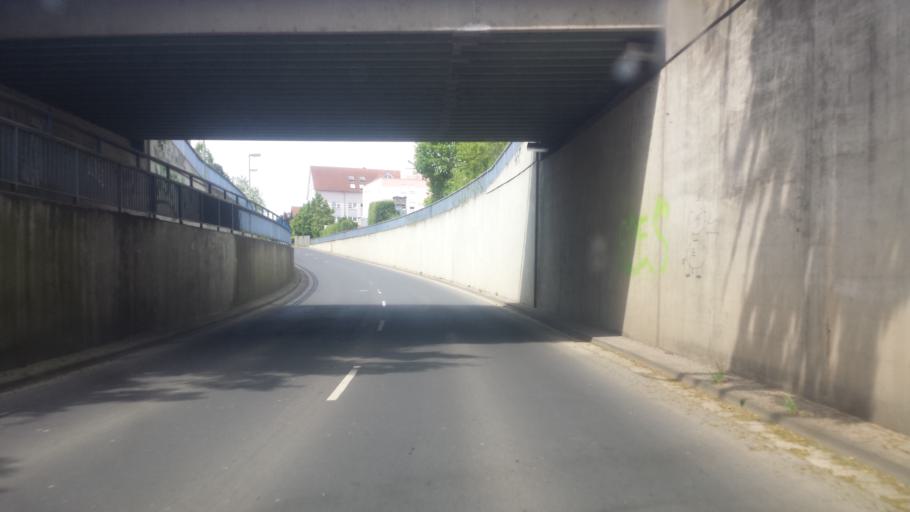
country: DE
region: Hesse
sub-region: Regierungsbezirk Darmstadt
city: Karben
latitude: 50.2103
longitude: 8.7538
